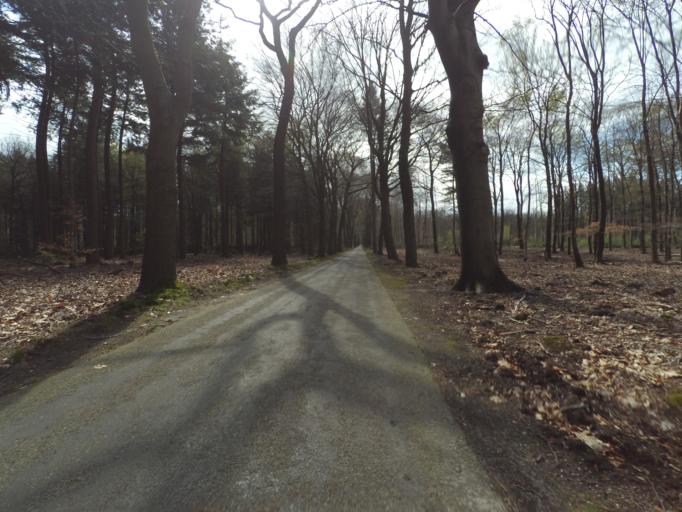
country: NL
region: Gelderland
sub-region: Gemeente Nunspeet
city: Nunspeet
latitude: 52.3570
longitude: 5.8534
